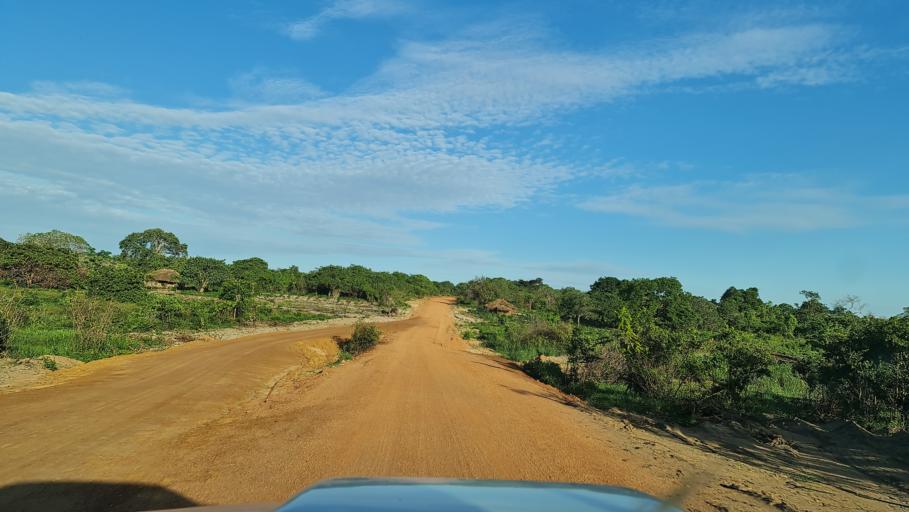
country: MZ
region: Nampula
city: Nacala
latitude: -14.6729
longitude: 40.2819
